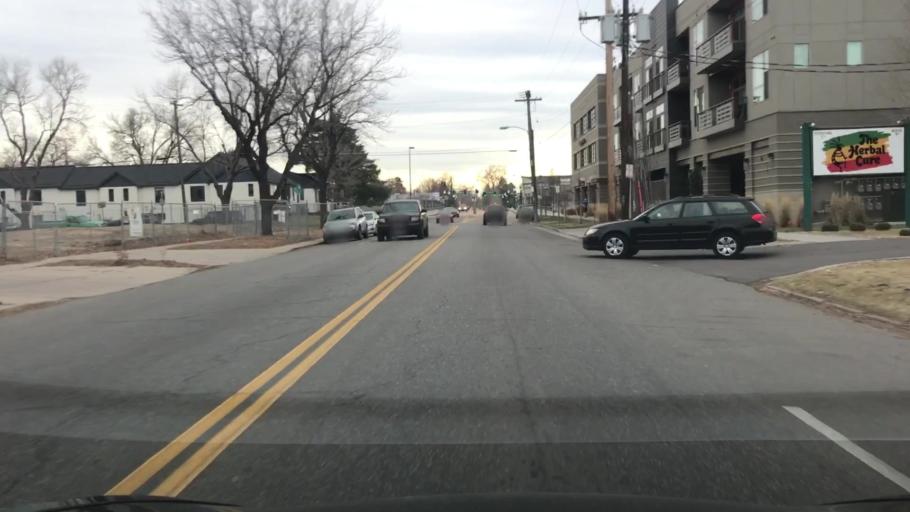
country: US
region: Colorado
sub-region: Denver County
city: Denver
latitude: 39.6991
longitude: -104.9828
